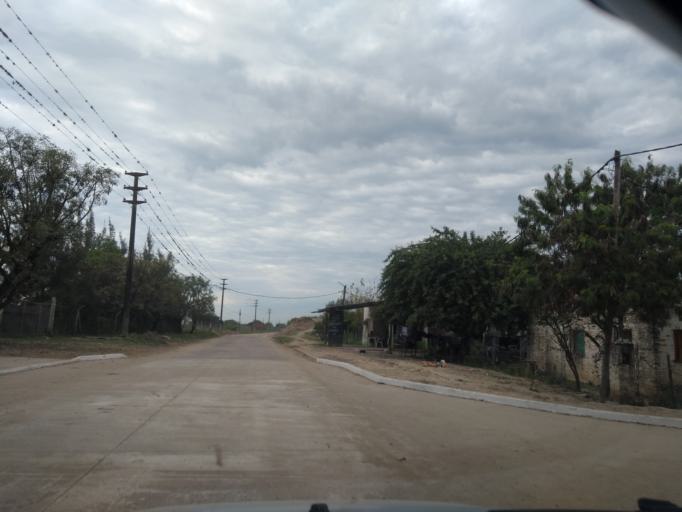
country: AR
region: Chaco
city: Puerto Vilelas
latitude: -27.5347
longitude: -58.9211
